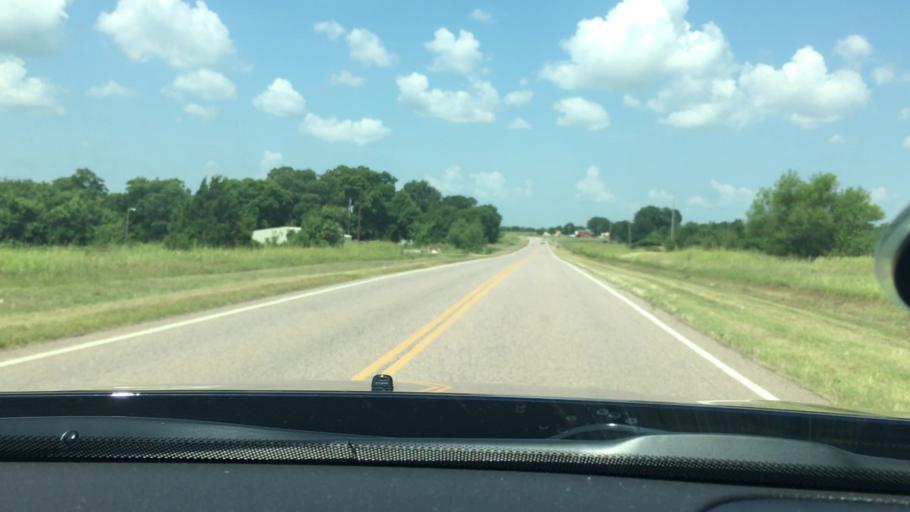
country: US
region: Oklahoma
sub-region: Bryan County
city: Durant
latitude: 34.0857
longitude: -96.3951
